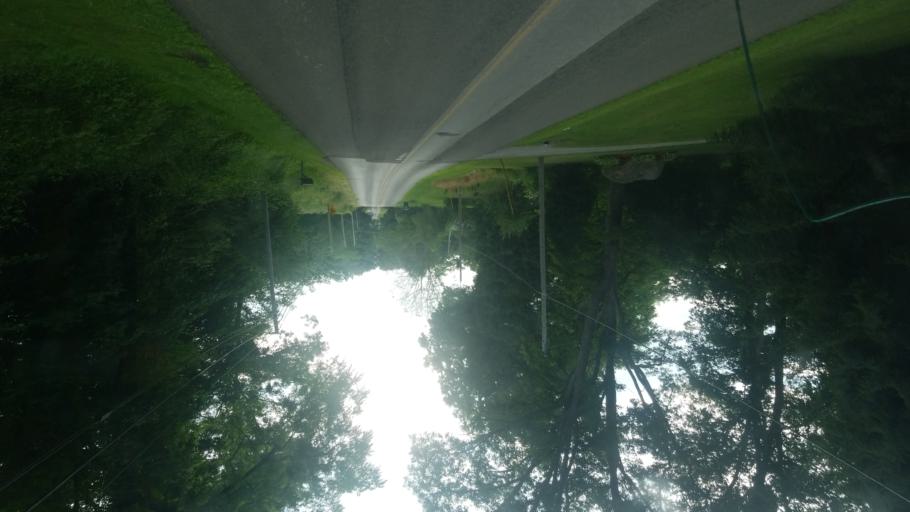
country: US
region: Ohio
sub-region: Wayne County
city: Wooster
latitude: 40.7847
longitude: -81.9852
